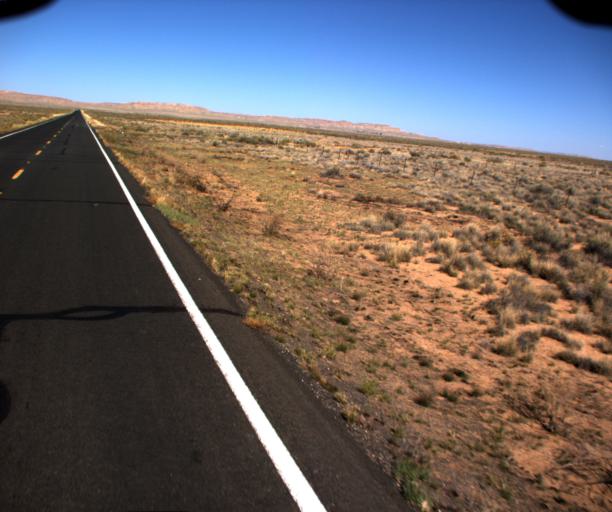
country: US
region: Arizona
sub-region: Navajo County
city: First Mesa
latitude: 35.7108
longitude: -110.5113
